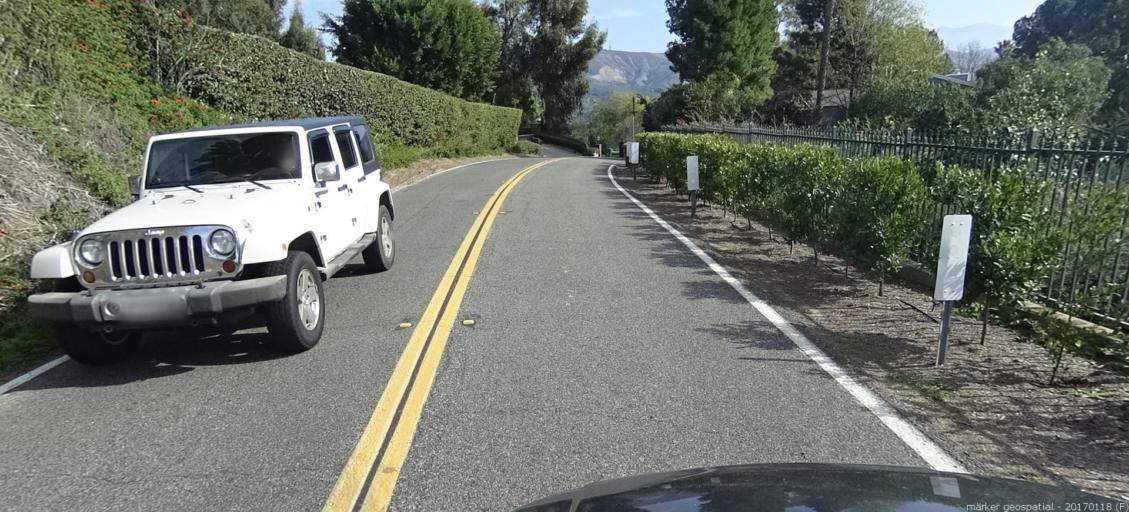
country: US
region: California
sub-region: Orange County
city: North Tustin
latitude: 33.7589
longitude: -117.7817
